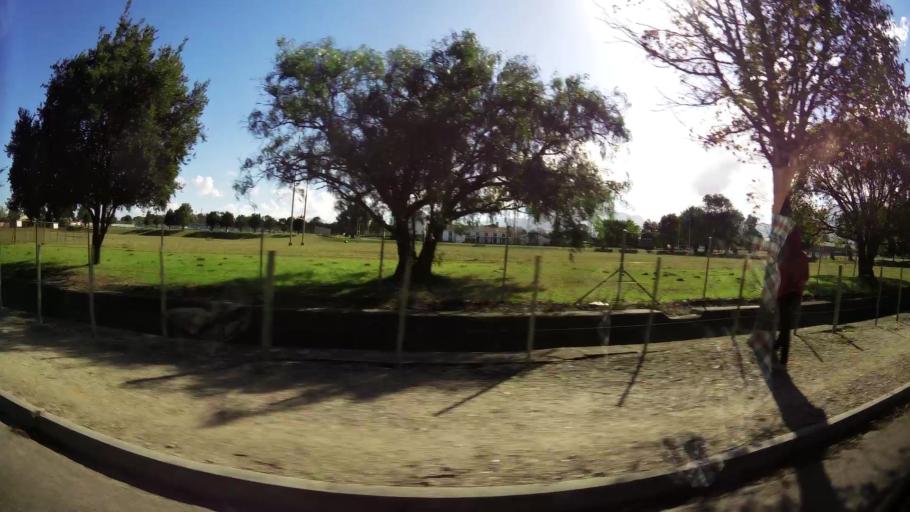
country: ZA
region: Western Cape
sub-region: Eden District Municipality
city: George
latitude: -33.9766
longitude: 22.4471
